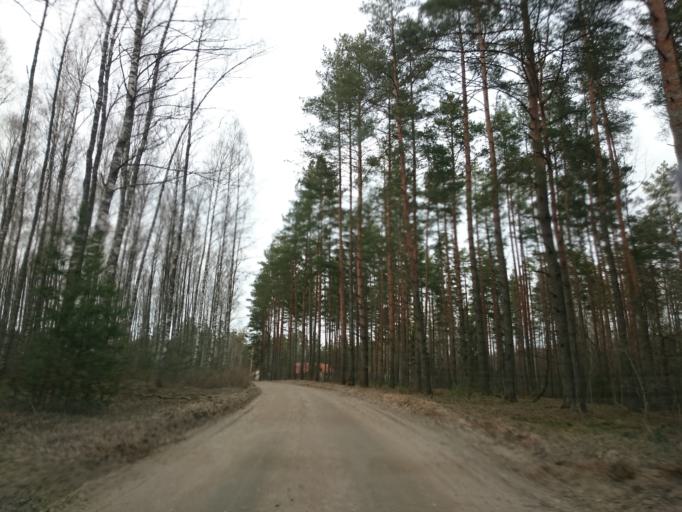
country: LV
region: Garkalne
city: Garkalne
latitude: 57.0233
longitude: 24.3866
